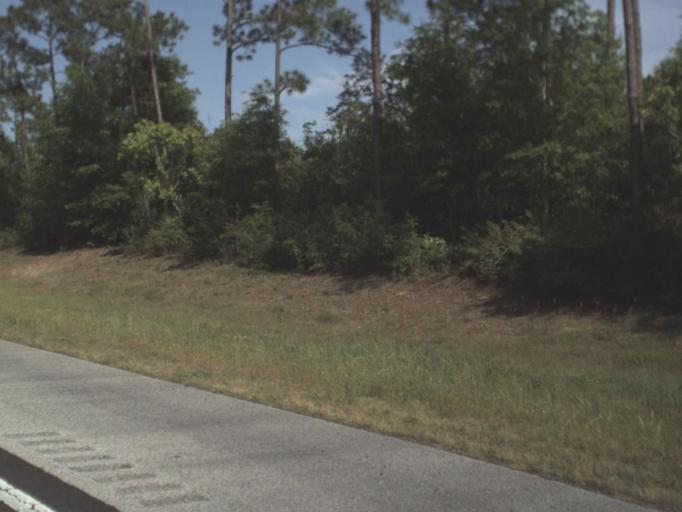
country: US
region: Florida
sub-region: Santa Rosa County
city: East Milton
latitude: 30.6335
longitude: -86.9244
